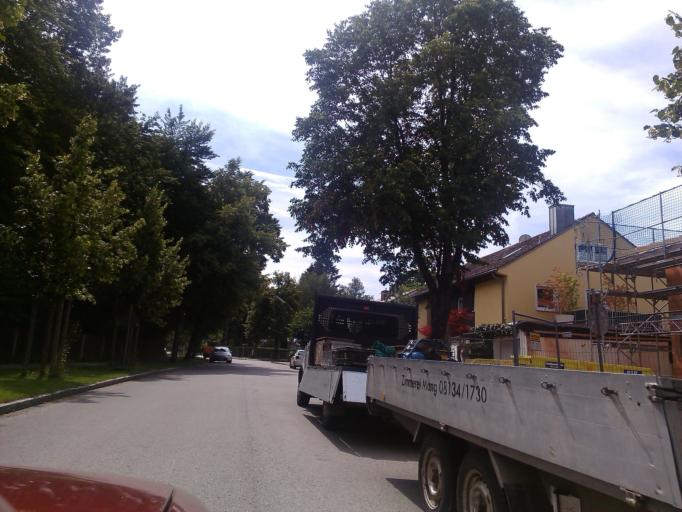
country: DE
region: Bavaria
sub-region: Upper Bavaria
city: Gauting
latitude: 48.0748
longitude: 11.3707
